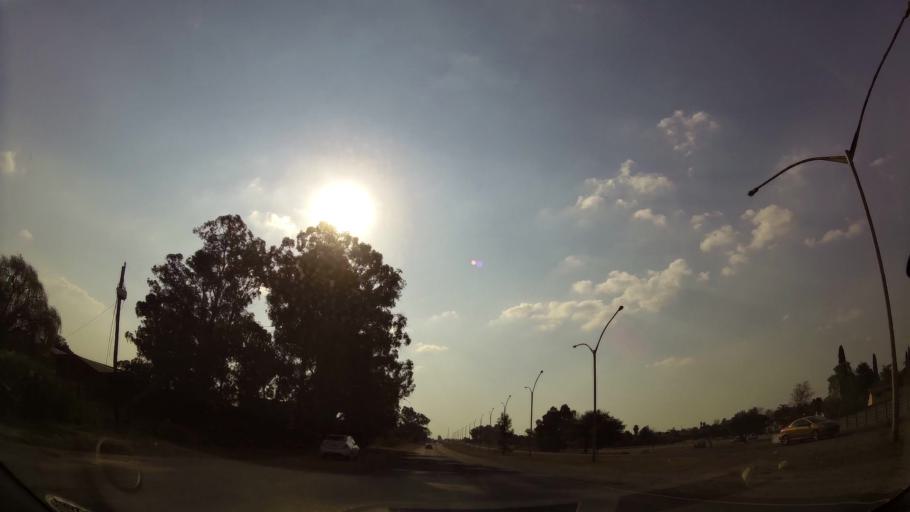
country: ZA
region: Gauteng
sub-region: Ekurhuleni Metropolitan Municipality
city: Benoni
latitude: -26.1339
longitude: 28.2912
